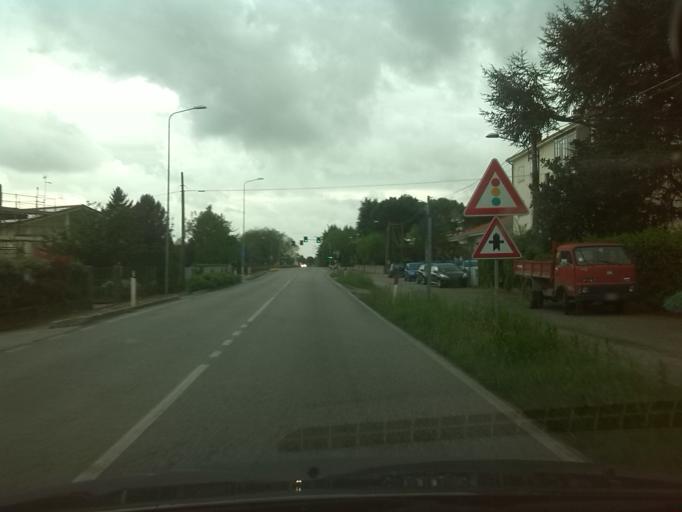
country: IT
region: Friuli Venezia Giulia
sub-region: Provincia di Gorizia
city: San Lorenzo Isontino
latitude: 45.9334
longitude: 13.5296
